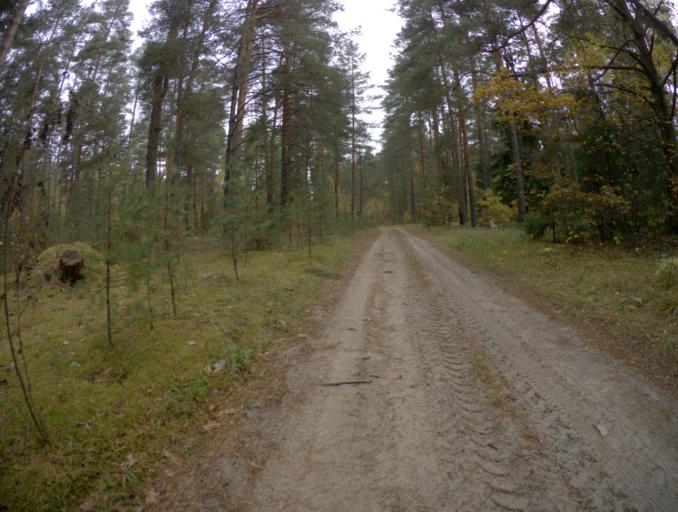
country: RU
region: Vladimir
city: Kommunar
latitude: 56.0527
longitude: 40.4603
